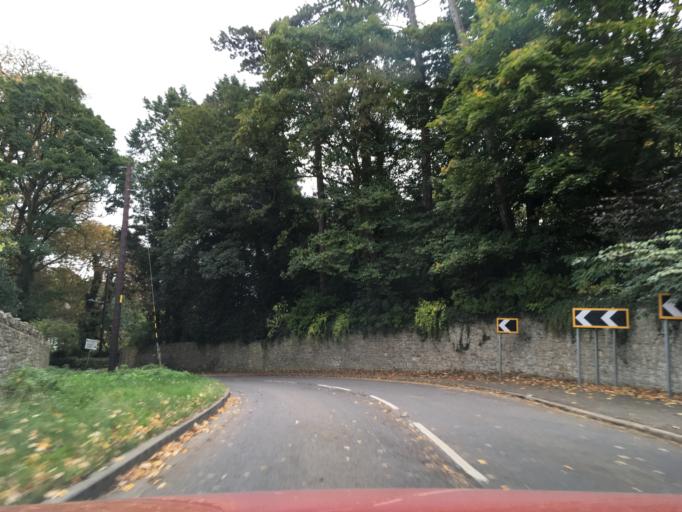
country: GB
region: England
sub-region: South Gloucestershire
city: Wickwar
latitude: 51.5967
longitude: -2.4038
